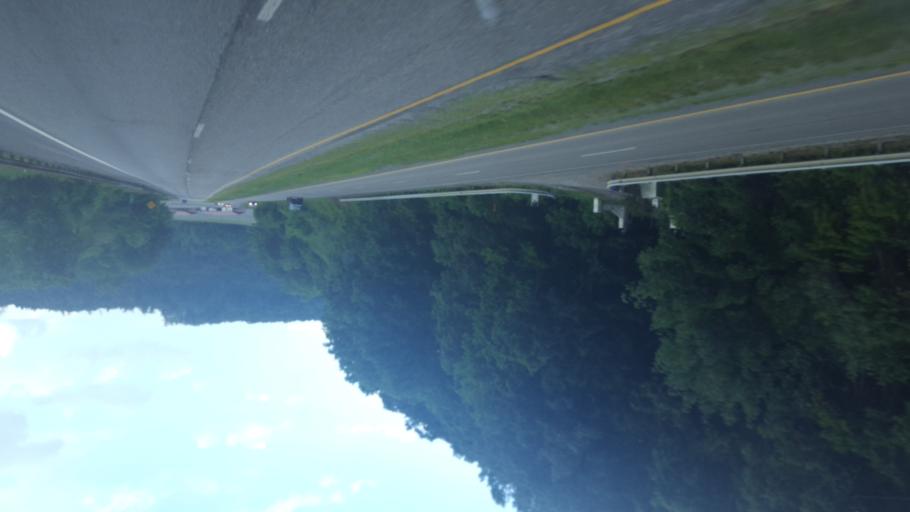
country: US
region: Virginia
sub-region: Wise County
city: Wise
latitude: 37.0135
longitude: -82.5913
